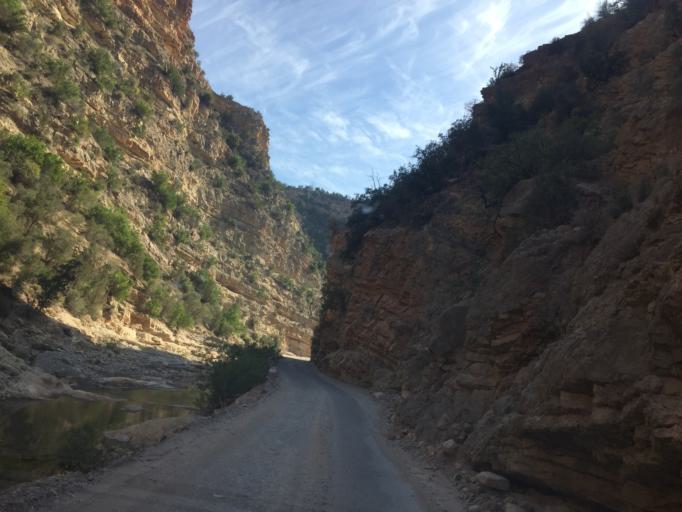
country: MA
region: Souss-Massa-Draa
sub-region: Agadir-Ida-ou-Tnan
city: Aourir
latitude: 30.5652
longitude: -9.5385
